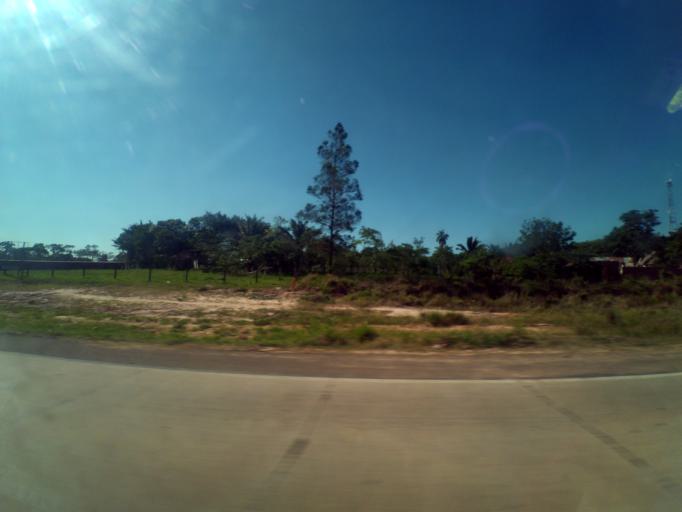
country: BO
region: Santa Cruz
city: Santa Cruz de la Sierra
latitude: -17.7750
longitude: -63.2465
